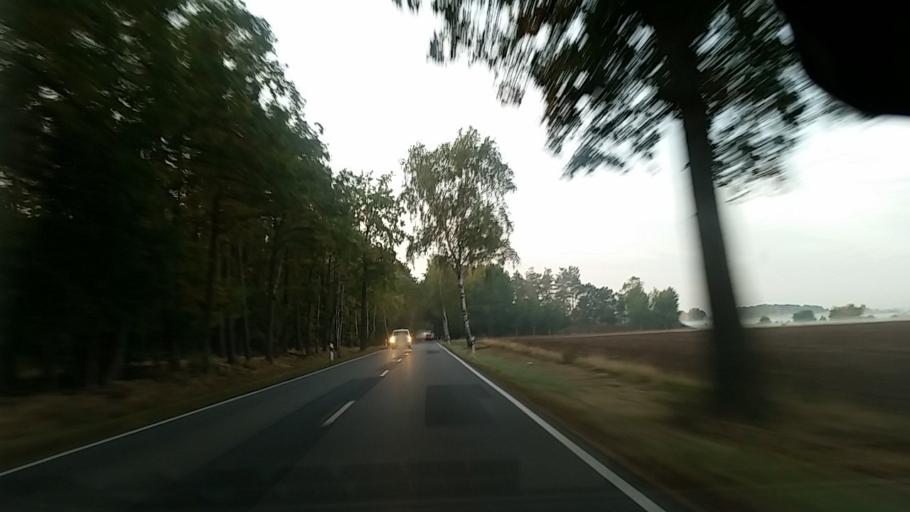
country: DE
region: Lower Saxony
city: Wittingen
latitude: 52.7753
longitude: 10.7134
